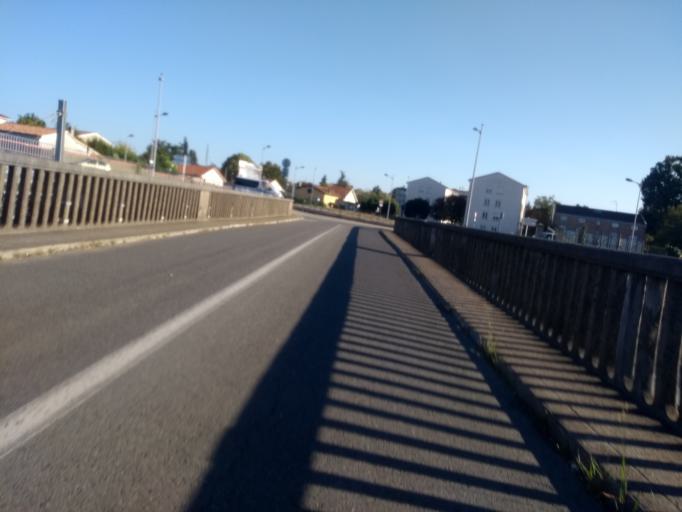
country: FR
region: Aquitaine
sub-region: Departement de la Gironde
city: Talence
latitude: 44.8154
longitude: -0.6035
